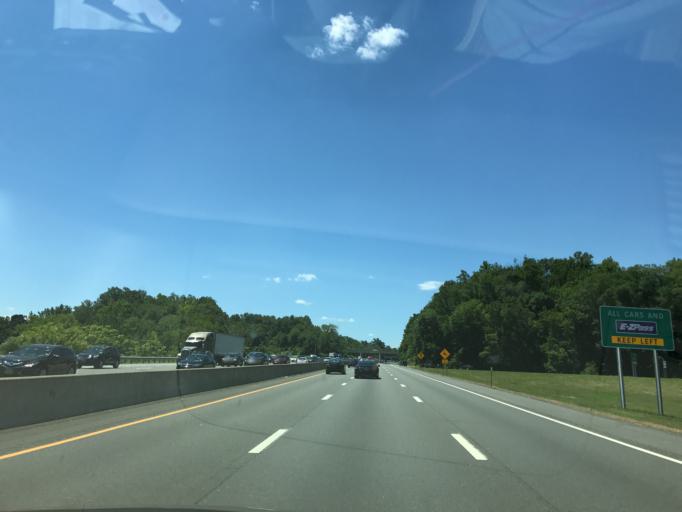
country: US
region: New York
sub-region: Rockland County
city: Spring Valley
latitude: 41.1001
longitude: -74.0345
